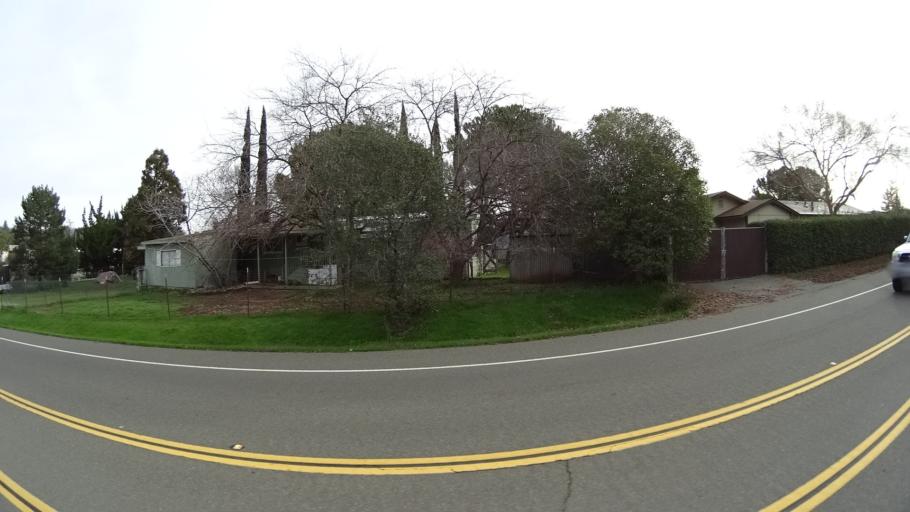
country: US
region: California
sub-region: Butte County
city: Oroville East
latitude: 39.5264
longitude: -121.4667
